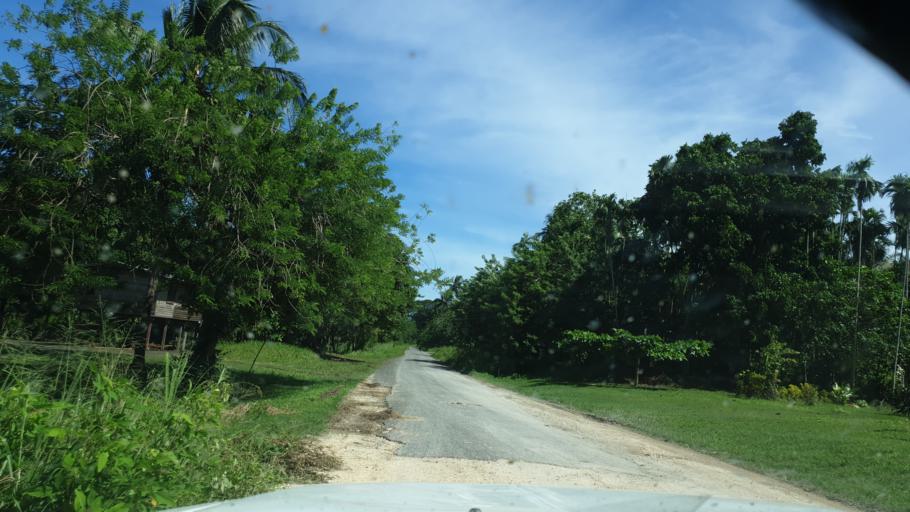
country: PG
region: Madang
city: Madang
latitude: -4.6890
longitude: 145.6047
